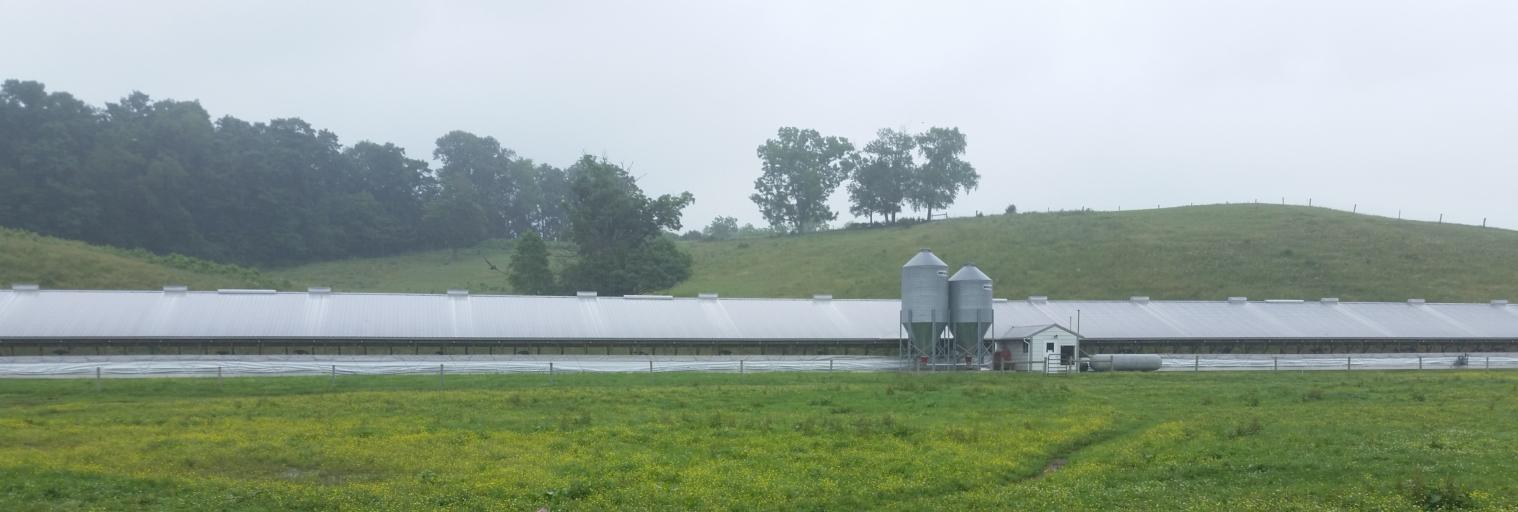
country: US
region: Ohio
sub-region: Holmes County
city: Millersburg
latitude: 40.4749
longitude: -81.8479
